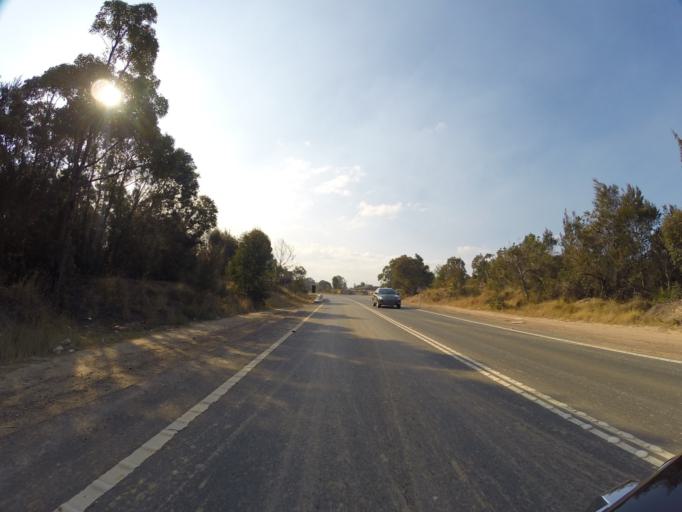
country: AU
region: New South Wales
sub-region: Sutherland Shire
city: Menai
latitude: -33.9940
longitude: 150.9967
